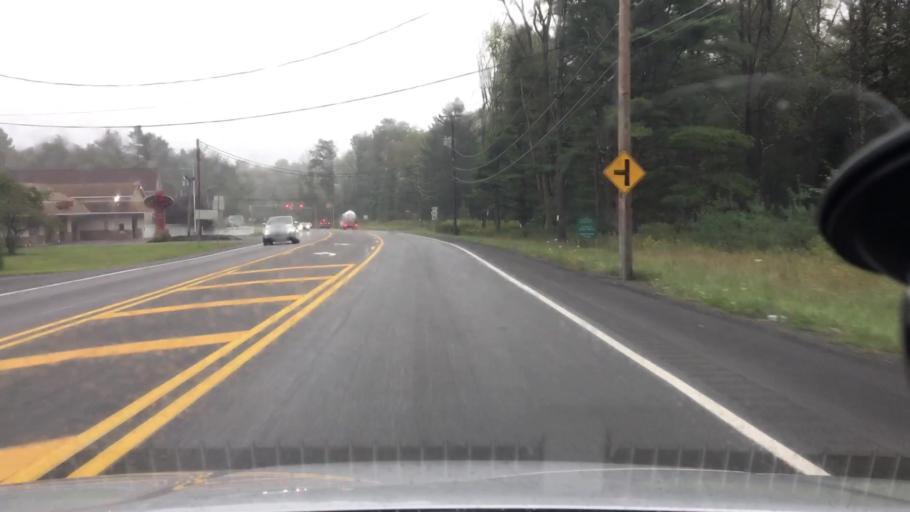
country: US
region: Pennsylvania
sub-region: Monroe County
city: Mount Pocono
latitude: 41.1270
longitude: -75.3063
